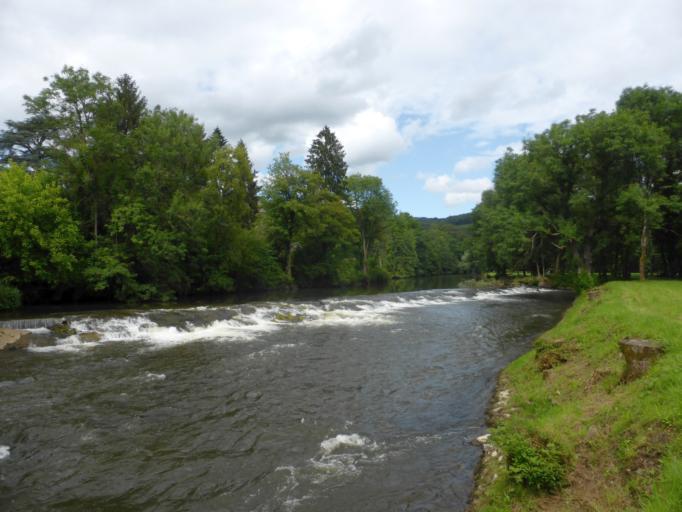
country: FR
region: Champagne-Ardenne
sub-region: Departement des Ardennes
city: Montherme
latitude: 49.8805
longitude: 4.7431
